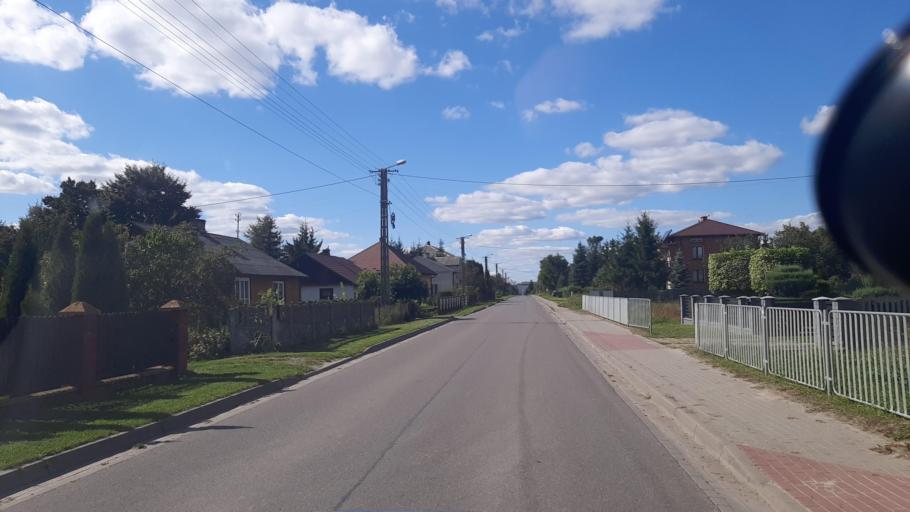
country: PL
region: Lublin Voivodeship
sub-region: Powiat lubartowski
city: Abramow
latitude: 51.4577
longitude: 22.3120
